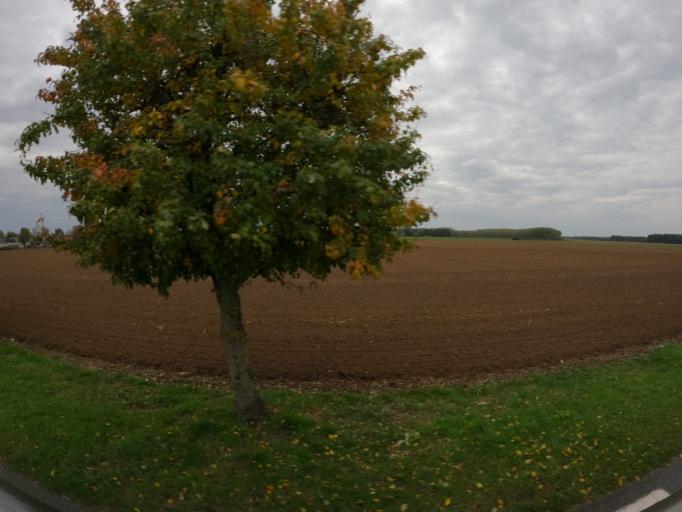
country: FR
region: Ile-de-France
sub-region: Departement de Seine-et-Marne
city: Villeneuve-le-Comte
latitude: 48.8169
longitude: 2.8222
